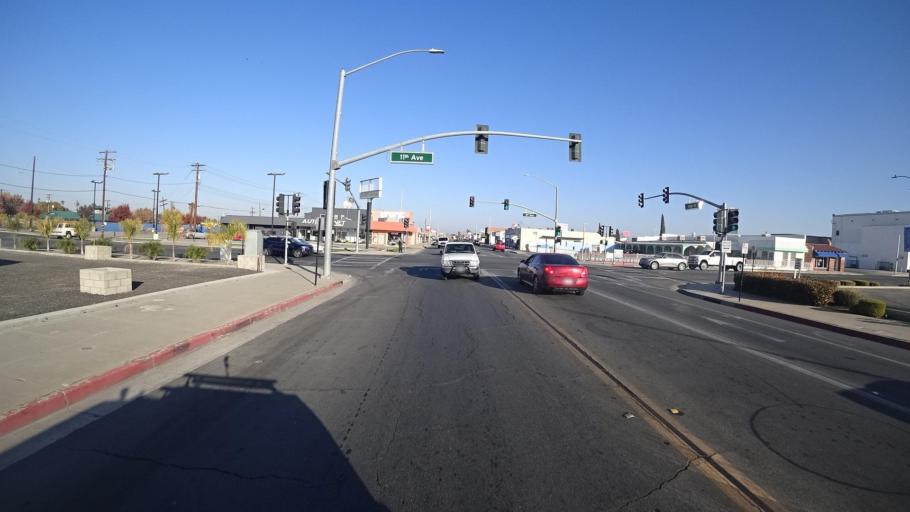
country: US
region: California
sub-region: Kern County
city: Delano
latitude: 35.7699
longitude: -119.2472
